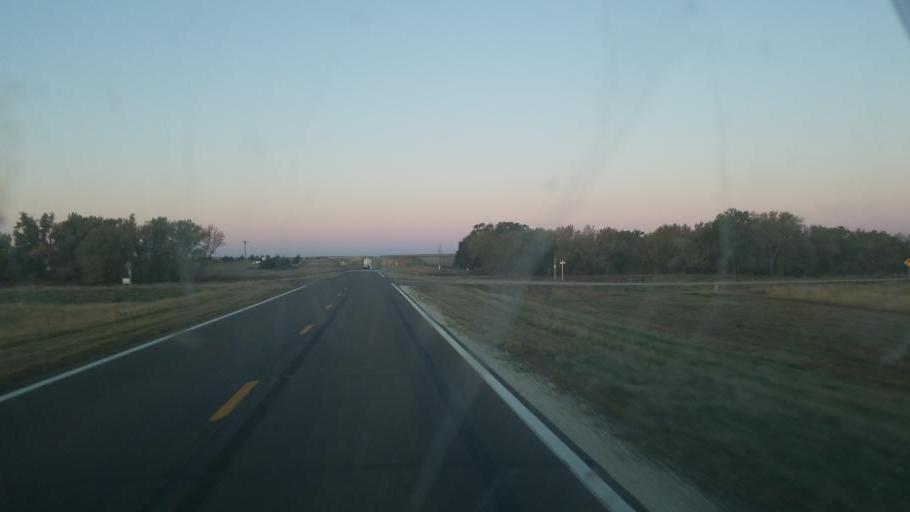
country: US
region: Kansas
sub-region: Wallace County
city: Sharon Springs
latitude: 38.9064
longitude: -101.6272
